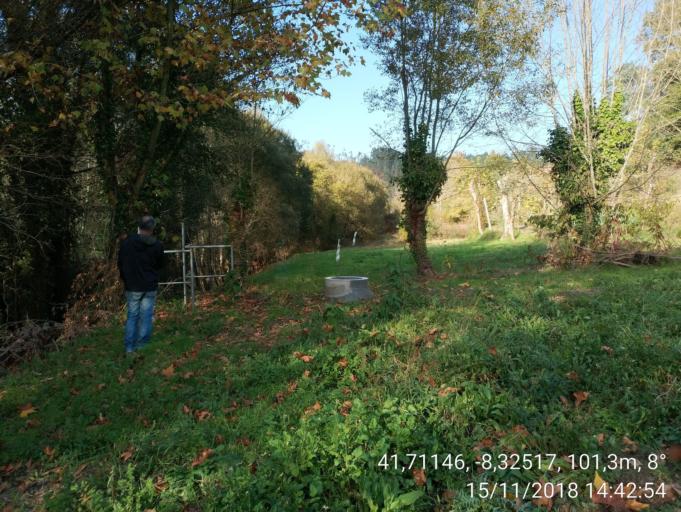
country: PT
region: Braga
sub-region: Terras de Bouro
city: Terras de Bouro
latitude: 41.7115
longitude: -8.3252
